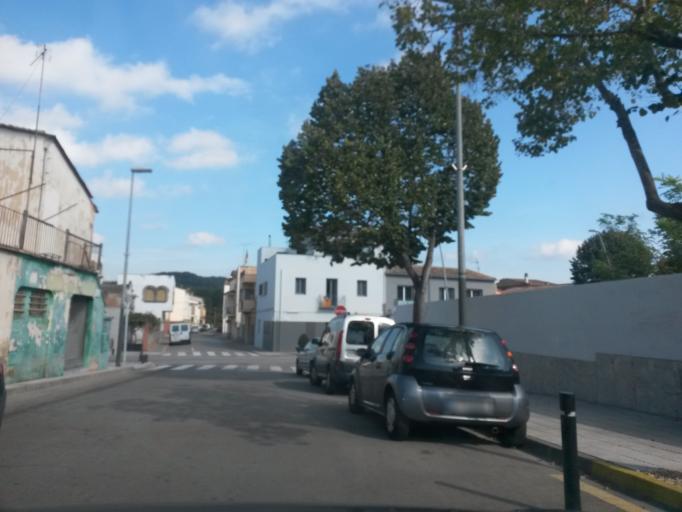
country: ES
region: Catalonia
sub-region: Provincia de Girona
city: Bescano
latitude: 41.9659
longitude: 2.7392
